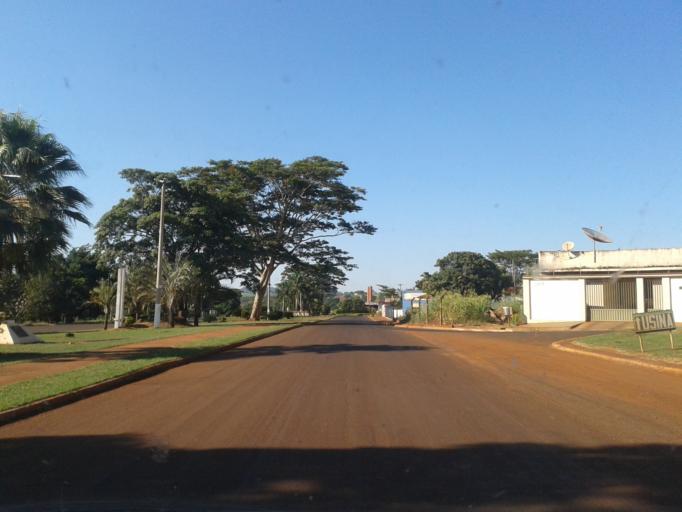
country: BR
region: Minas Gerais
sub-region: Capinopolis
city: Capinopolis
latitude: -18.6874
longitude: -49.5634
